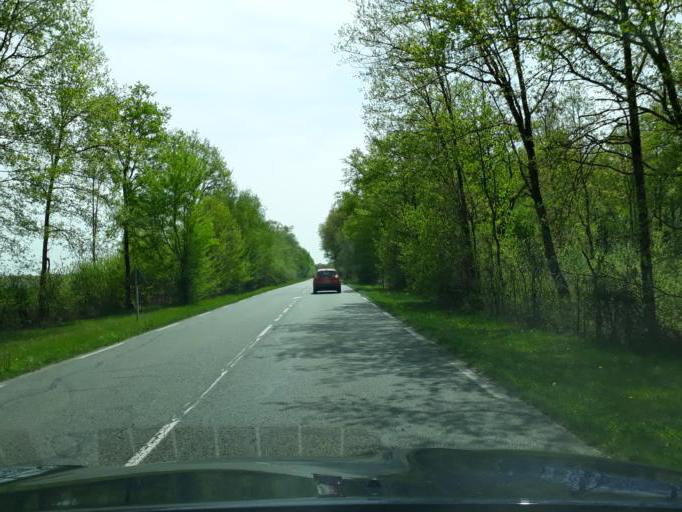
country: FR
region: Ile-de-France
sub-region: Departement des Yvelines
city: Saint-Leger-en-Yvelines
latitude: 48.7025
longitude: 1.7697
